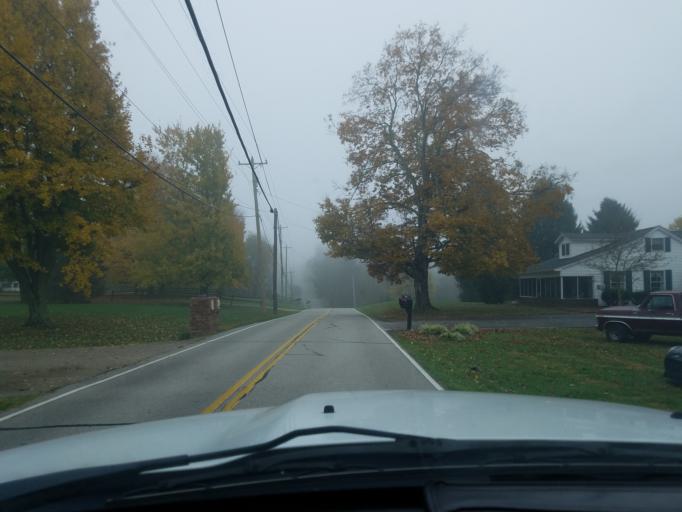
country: US
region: Indiana
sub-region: Floyd County
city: Georgetown
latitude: 38.3068
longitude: -85.9323
